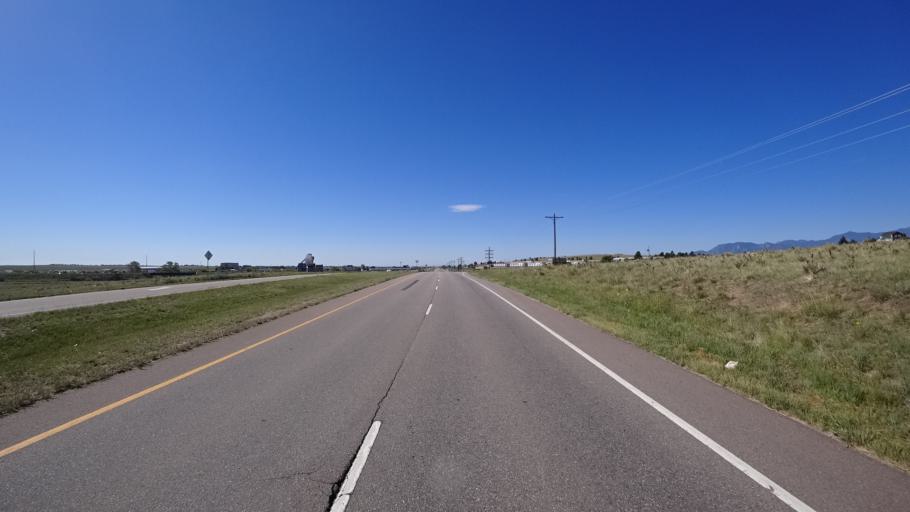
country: US
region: Colorado
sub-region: El Paso County
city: Cimarron Hills
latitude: 38.8889
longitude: -104.6829
